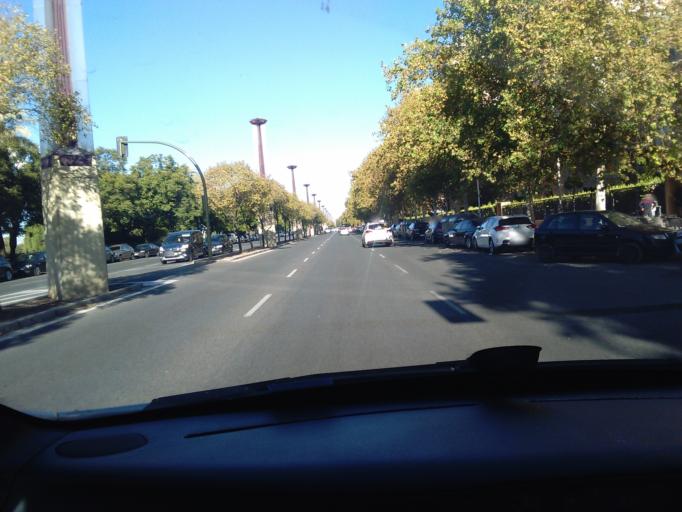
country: ES
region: Andalusia
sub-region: Provincia de Sevilla
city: Sevilla
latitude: 37.4074
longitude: -5.9926
